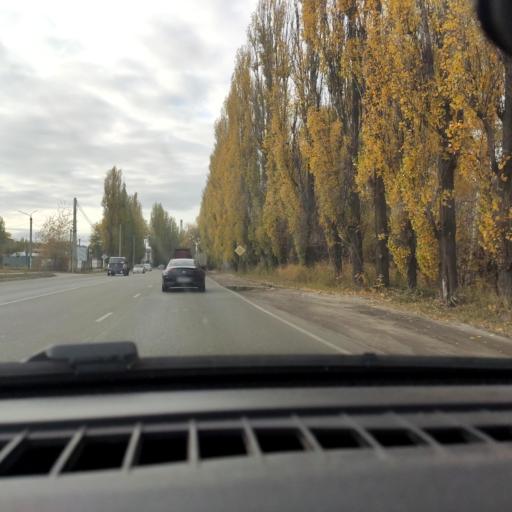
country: RU
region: Voronezj
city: Maslovka
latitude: 51.6225
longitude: 39.2484
